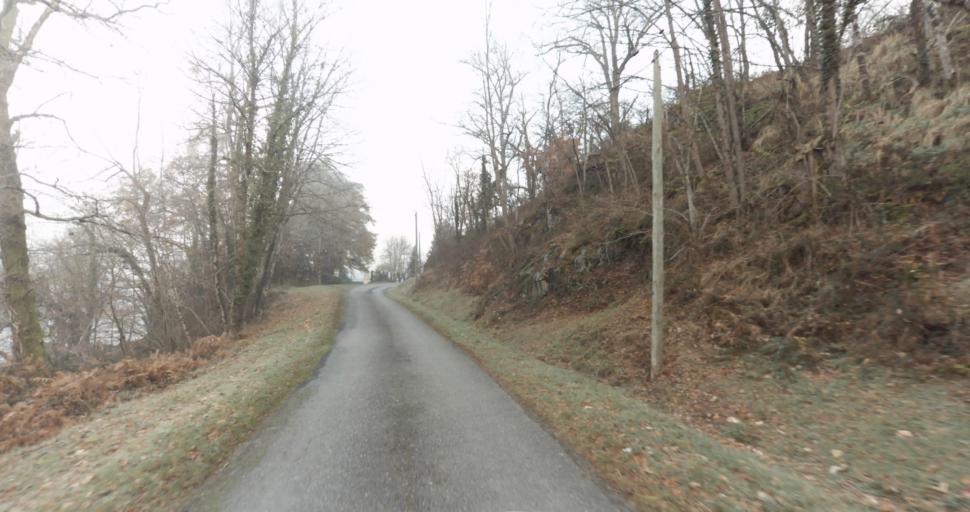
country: FR
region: Limousin
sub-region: Departement de la Haute-Vienne
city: Saint-Priest-sous-Aixe
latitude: 45.8173
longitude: 1.1197
